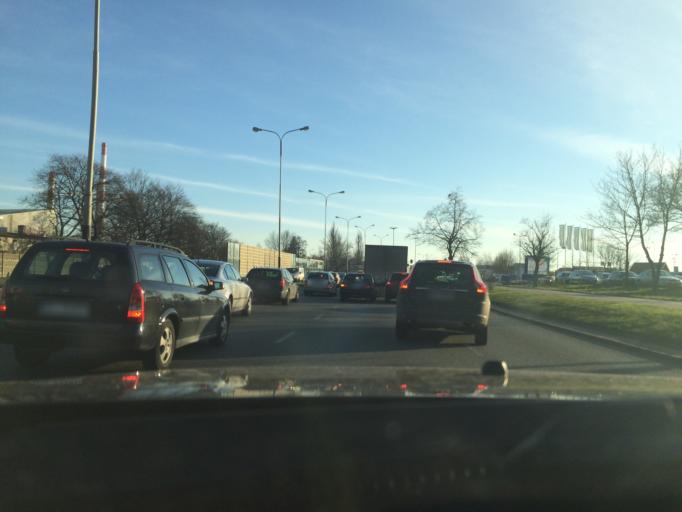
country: PL
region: Lodz Voivodeship
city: Lodz
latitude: 51.7468
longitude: 19.4394
